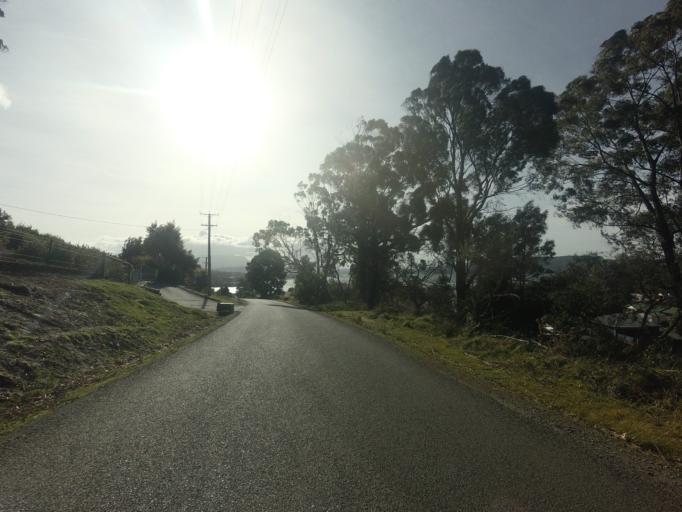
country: AU
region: Tasmania
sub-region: Kingborough
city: Margate
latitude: -43.0761
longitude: 147.2662
